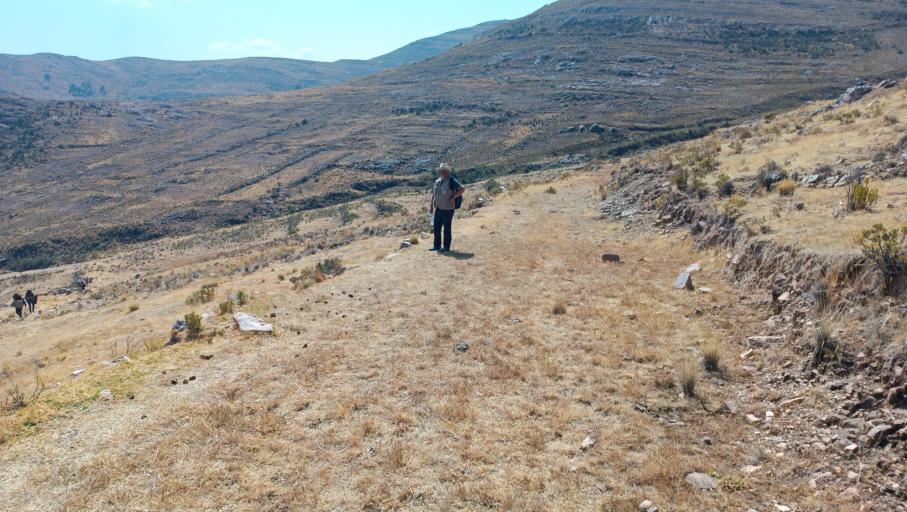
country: BO
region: La Paz
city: Batallas
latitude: -16.3466
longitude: -68.6580
